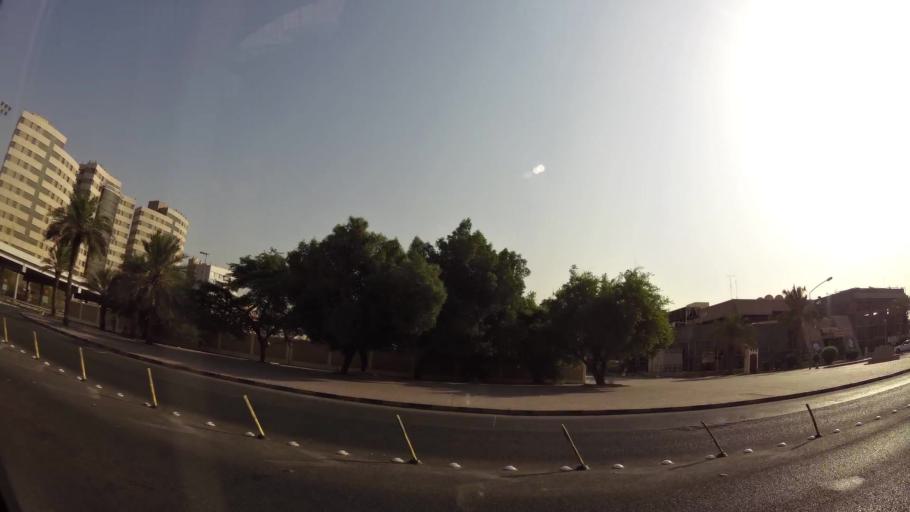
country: KW
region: Muhafazat Hawalli
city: Hawalli
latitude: 29.3275
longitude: 48.0294
